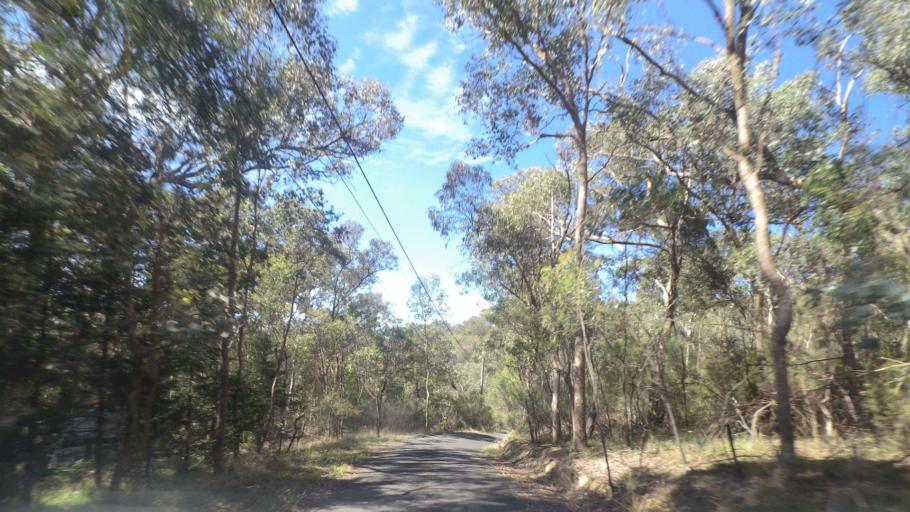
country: AU
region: Victoria
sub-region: Manningham
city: Warrandyte
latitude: -37.7482
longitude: 145.2250
